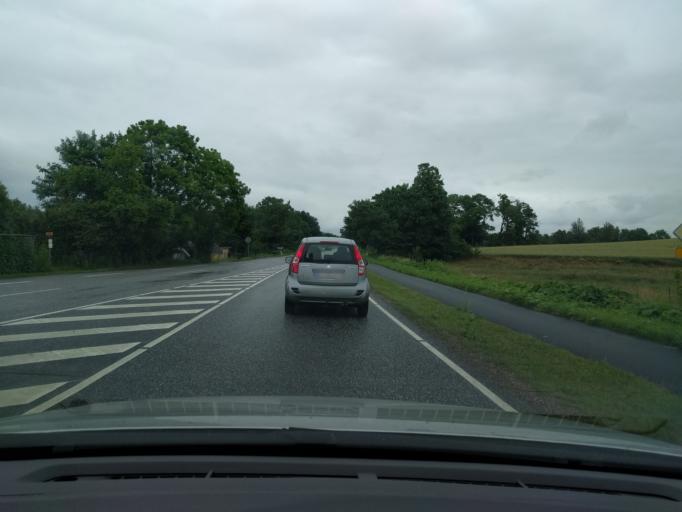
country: DK
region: Zealand
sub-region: Lejre Kommune
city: Osted
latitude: 55.5704
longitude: 11.9775
